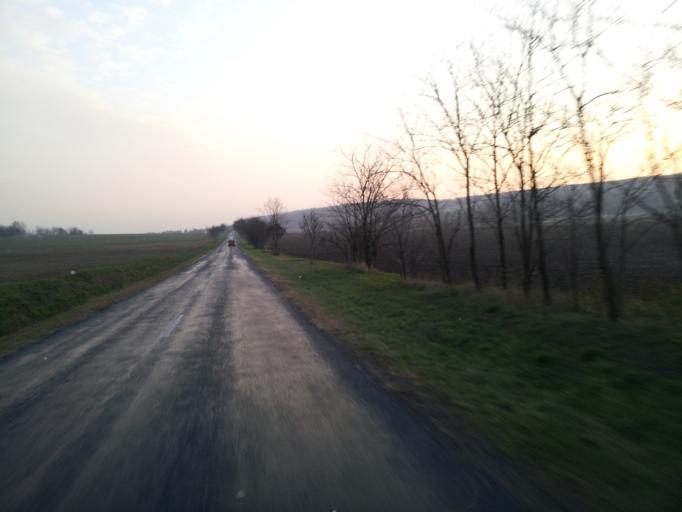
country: HU
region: Zala
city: Cserszegtomaj
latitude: 46.8384
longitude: 17.1962
